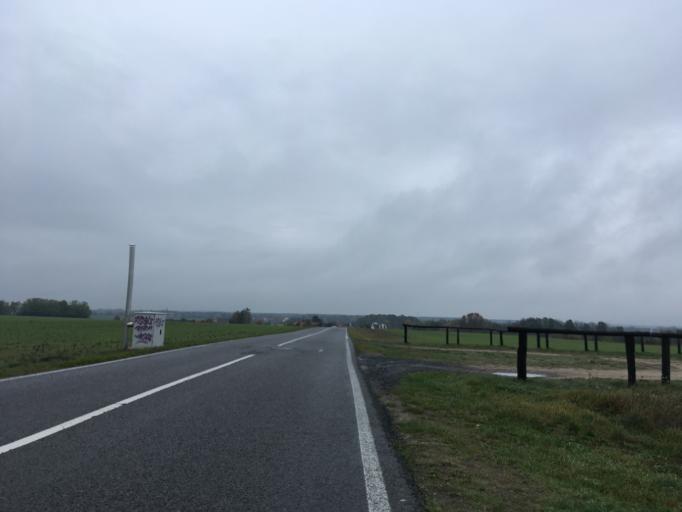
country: DE
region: Brandenburg
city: Tauche
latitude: 52.0681
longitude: 14.1851
